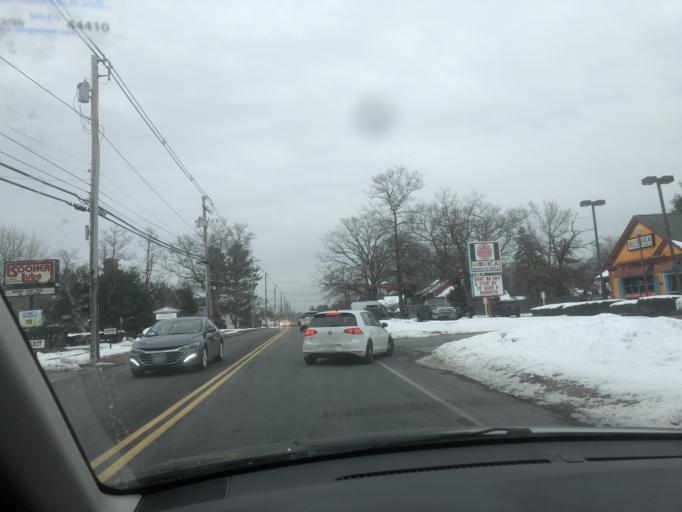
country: US
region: Massachusetts
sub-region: Middlesex County
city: Tewksbury
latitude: 42.6160
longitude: -71.2444
